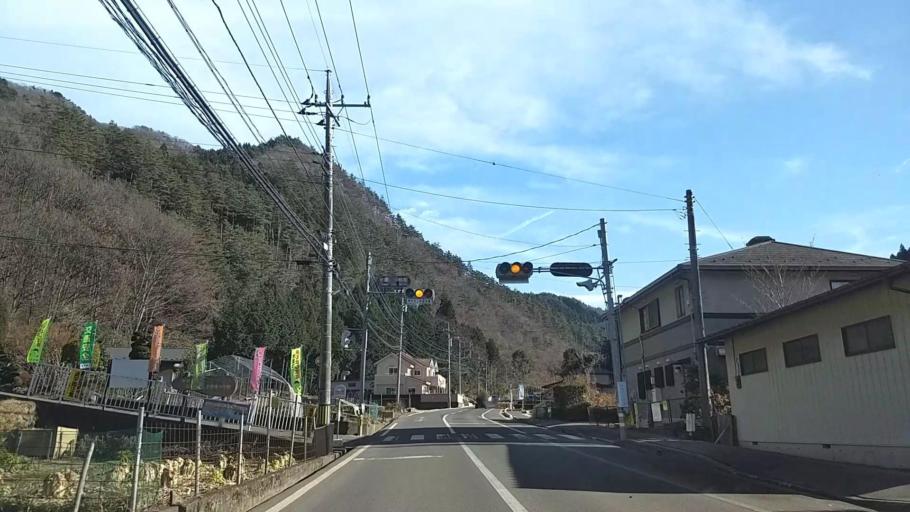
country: JP
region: Yamanashi
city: Otsuki
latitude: 35.5280
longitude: 138.9206
